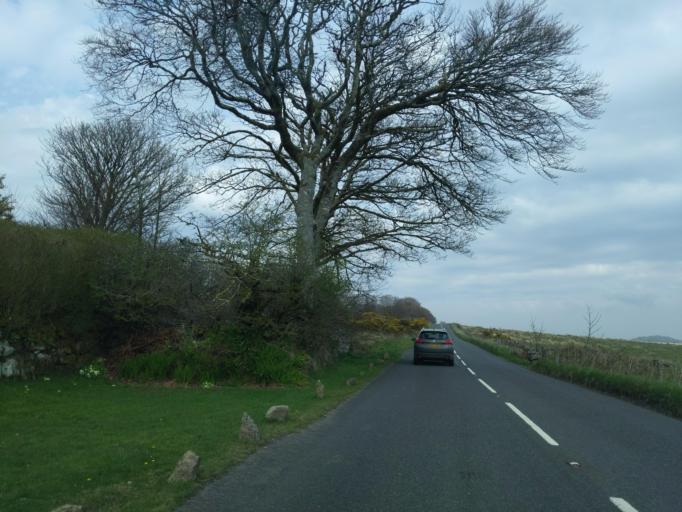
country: GB
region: England
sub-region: Devon
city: Yelverton
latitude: 50.5641
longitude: -3.9521
